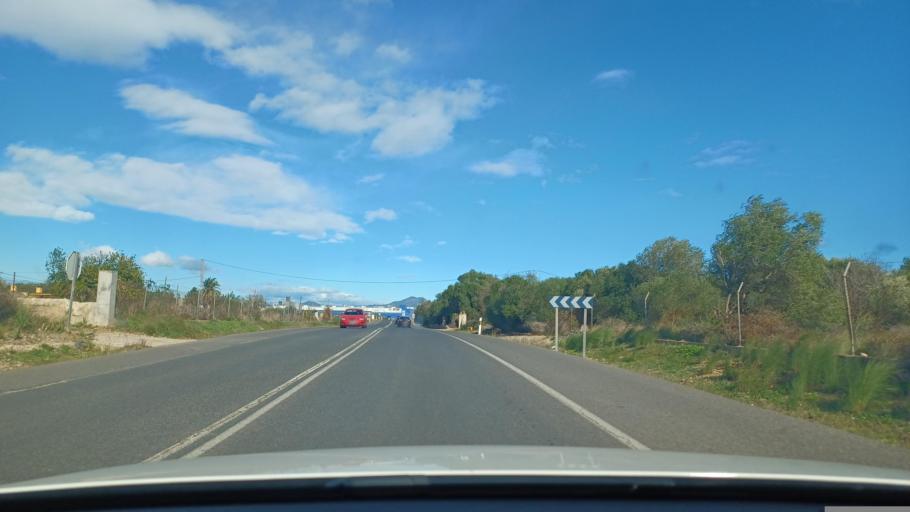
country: ES
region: Valencia
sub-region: Provincia de Castello
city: Vinaros
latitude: 40.4482
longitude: 0.4494
